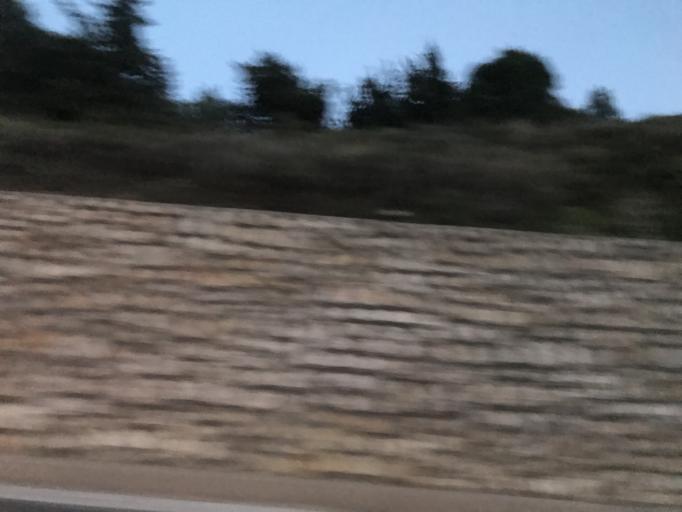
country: TR
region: Hatay
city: Samankaya
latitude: 36.1654
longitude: 36.1039
